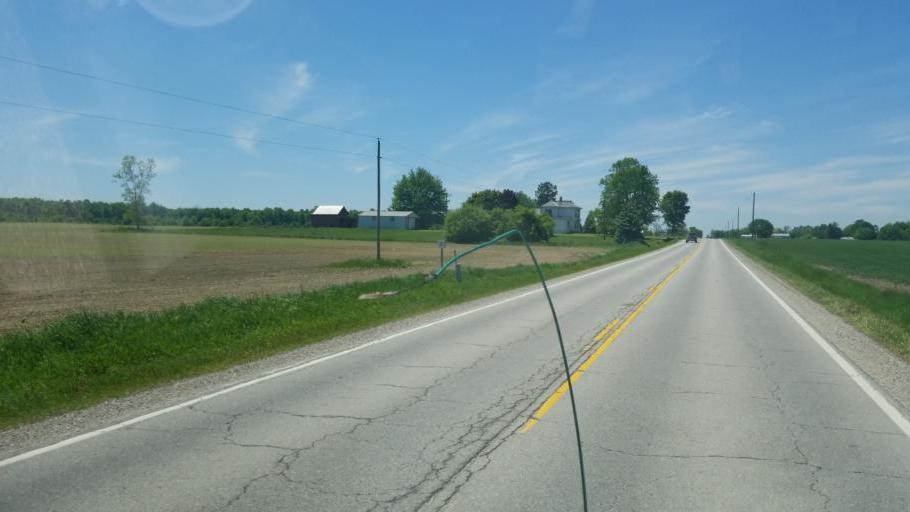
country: US
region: Ohio
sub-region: Huron County
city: New London
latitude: 41.0292
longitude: -82.4399
